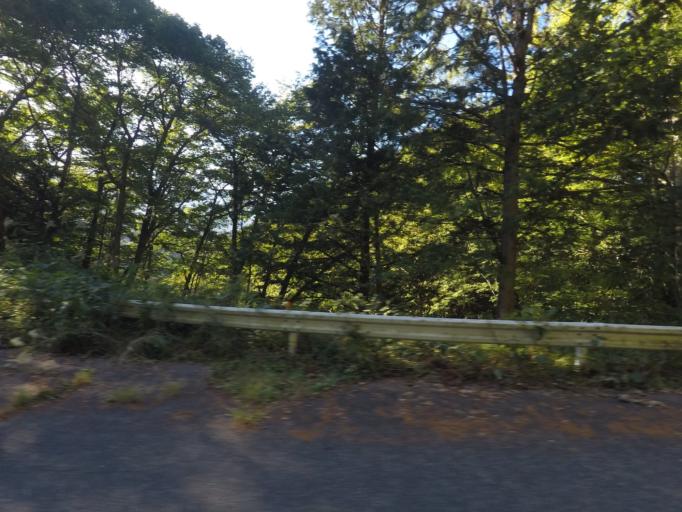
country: JP
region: Nagano
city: Tatsuno
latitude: 35.9660
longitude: 137.7744
